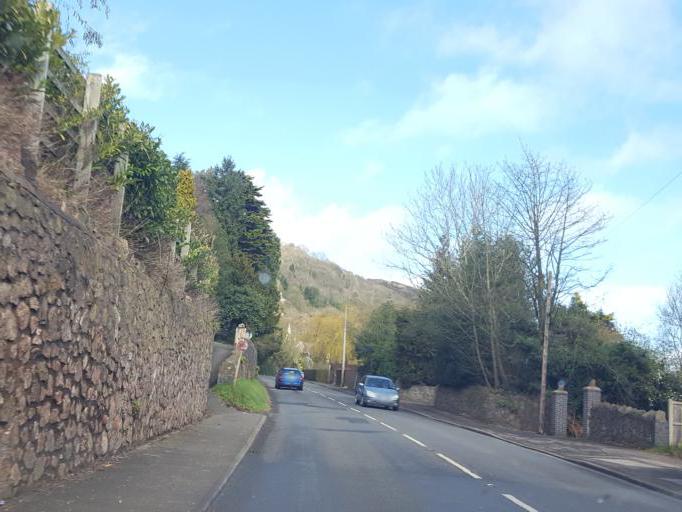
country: GB
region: England
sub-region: Worcestershire
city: Great Malvern
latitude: 52.0885
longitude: -2.3334
